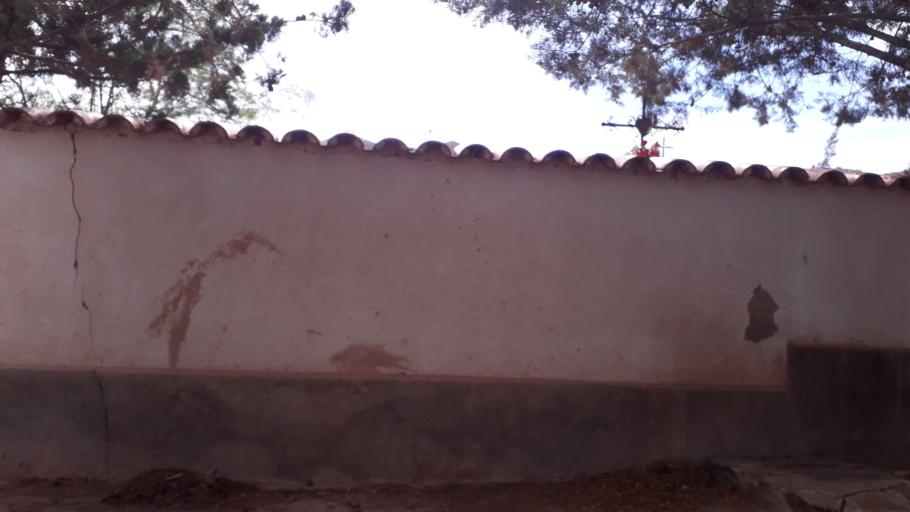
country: AR
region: Jujuy
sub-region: Departamento de Humahuaca
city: Humahuaca
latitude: -23.3043
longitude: -65.3587
